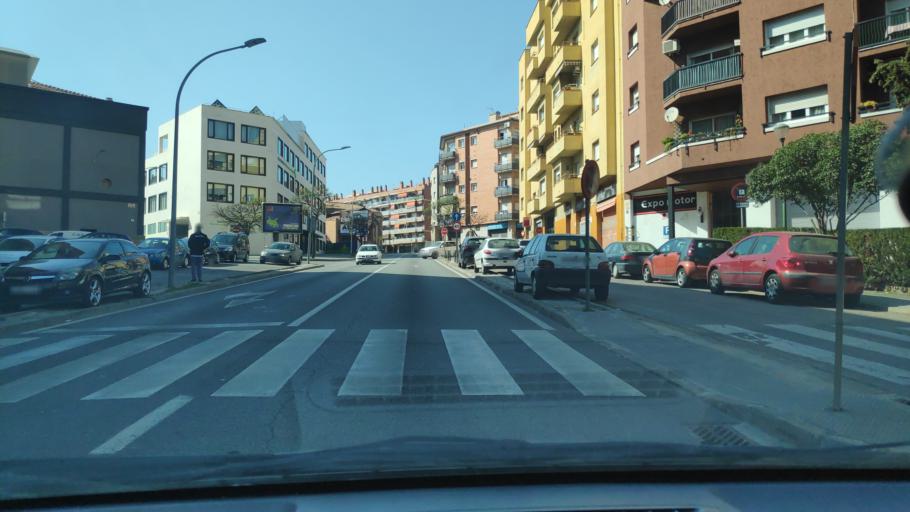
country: ES
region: Catalonia
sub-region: Provincia de Barcelona
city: Sabadell
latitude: 41.5345
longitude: 2.1178
